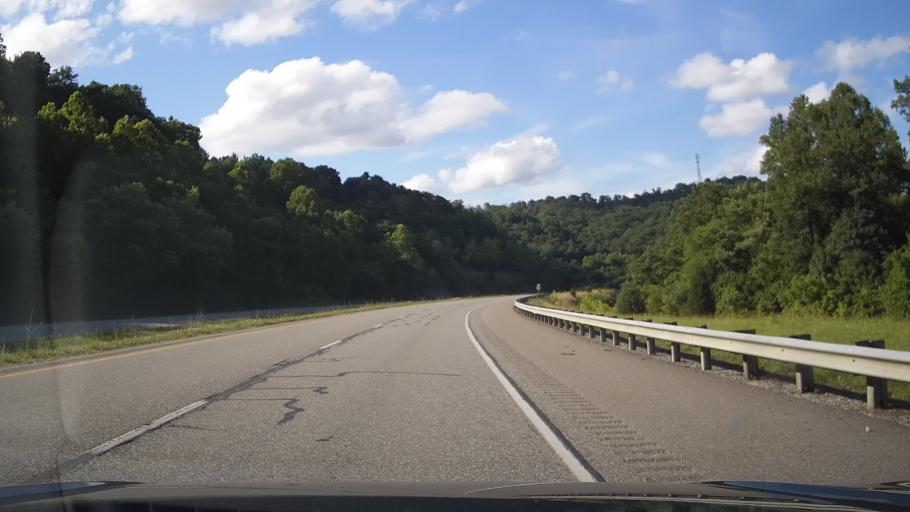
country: US
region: Kentucky
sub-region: Lawrence County
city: Louisa
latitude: 38.1643
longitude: -82.6454
